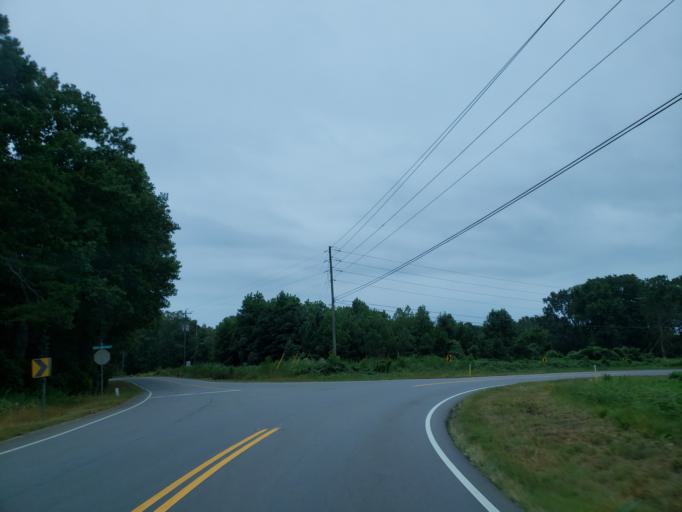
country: US
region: Georgia
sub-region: Cherokee County
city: Ball Ground
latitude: 34.3287
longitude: -84.4687
